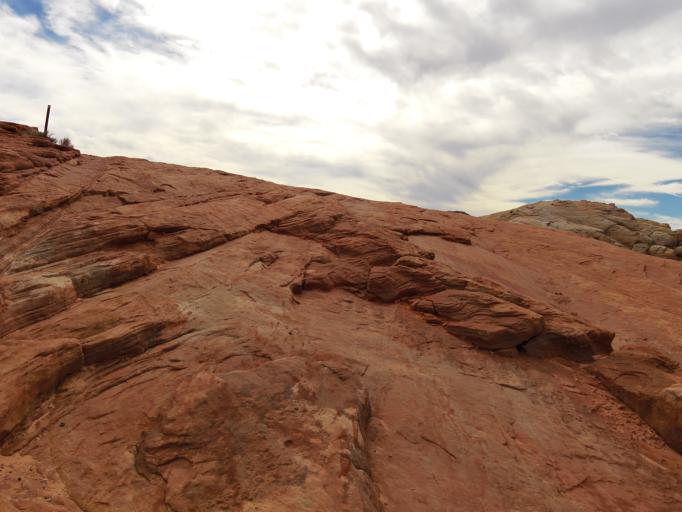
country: US
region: Nevada
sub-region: Clark County
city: Moapa Valley
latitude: 36.4851
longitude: -114.5224
